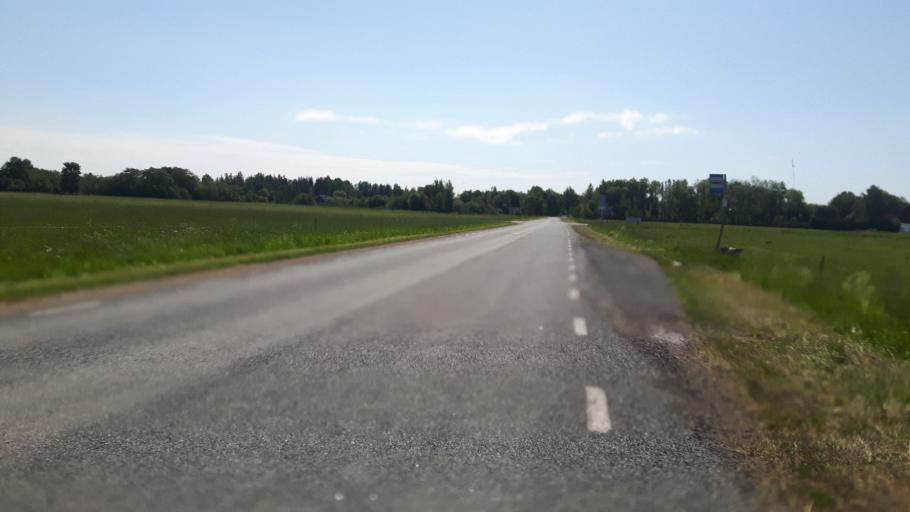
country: EE
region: Paernumaa
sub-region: Vaendra vald (alev)
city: Vandra
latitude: 58.5943
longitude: 25.0246
